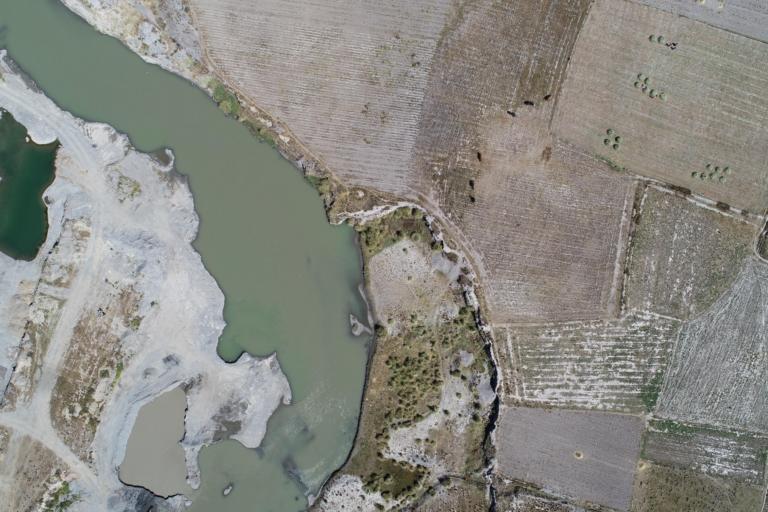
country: BO
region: La Paz
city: Achacachi
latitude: -16.0402
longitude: -68.6968
